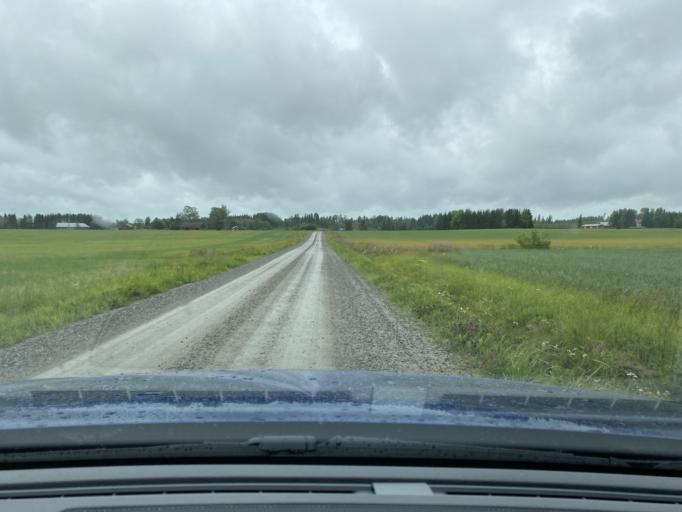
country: FI
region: Pirkanmaa
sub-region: Lounais-Pirkanmaa
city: Punkalaidun
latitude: 61.1492
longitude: 23.2239
